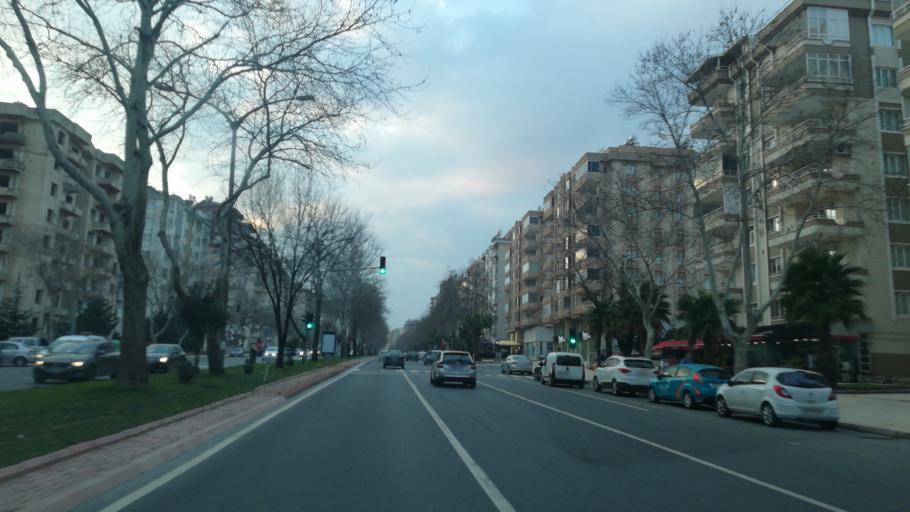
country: TR
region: Kahramanmaras
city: Kahramanmaras
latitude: 37.5872
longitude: 36.8944
